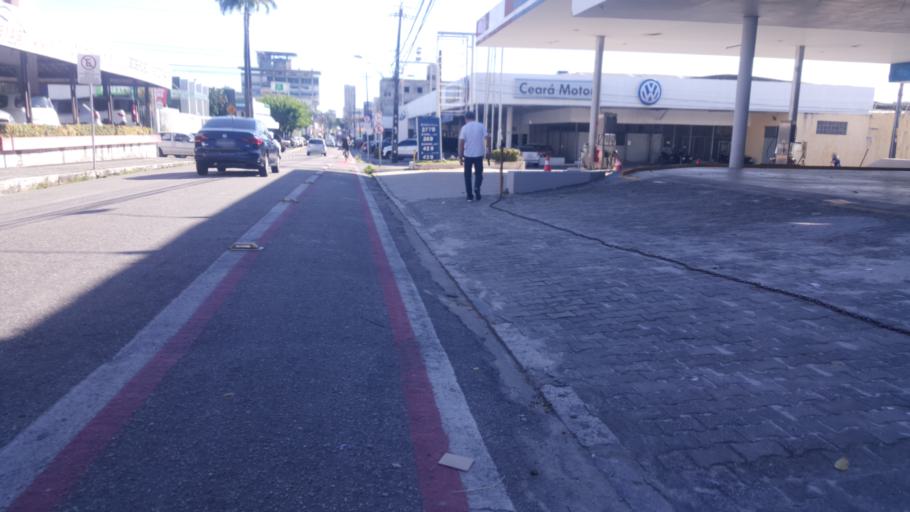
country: BR
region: Ceara
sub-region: Fortaleza
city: Fortaleza
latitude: -3.7404
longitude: -38.5327
